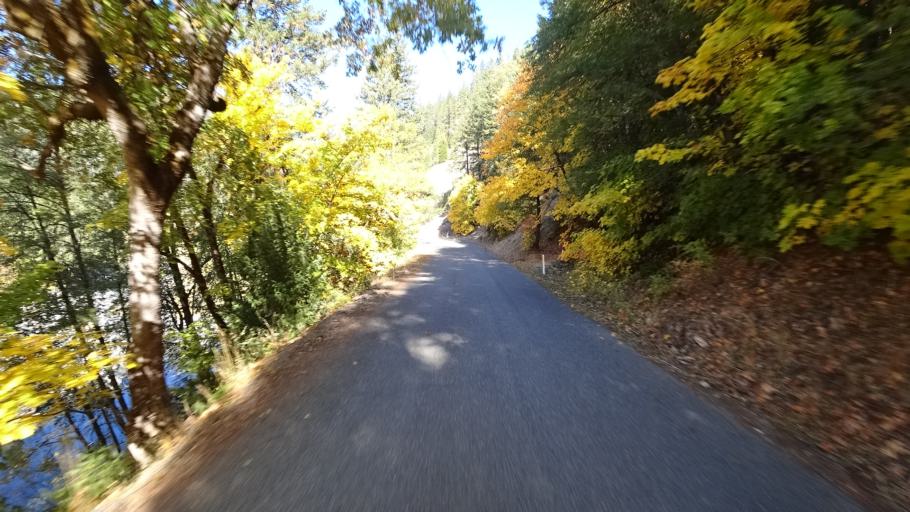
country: US
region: California
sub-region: Siskiyou County
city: Happy Camp
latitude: 41.6426
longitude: -123.1107
